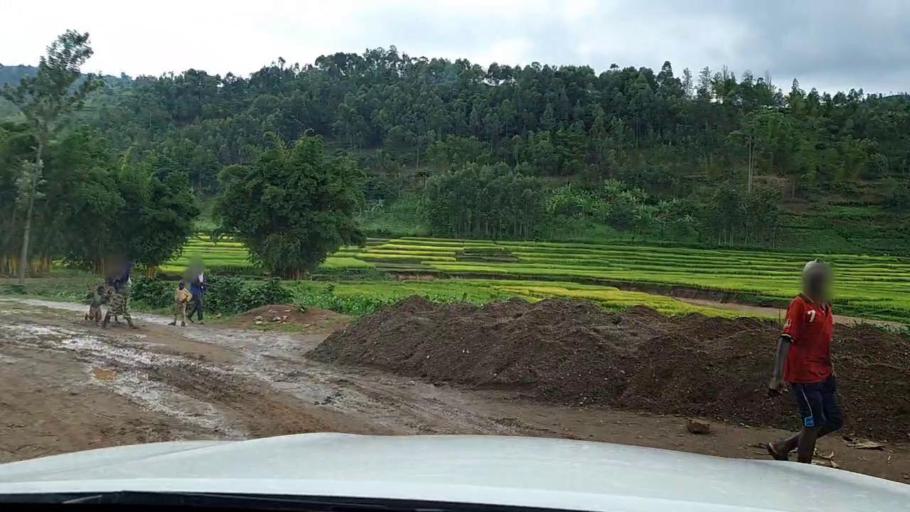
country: RW
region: Western Province
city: Cyangugu
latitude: -2.5656
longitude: 29.0351
